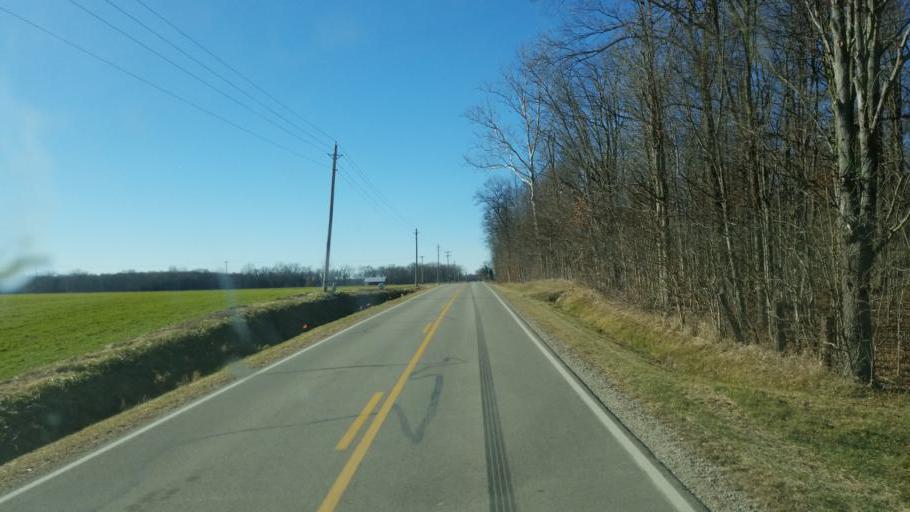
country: US
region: Ohio
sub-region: Crawford County
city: Galion
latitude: 40.7342
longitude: -82.8458
